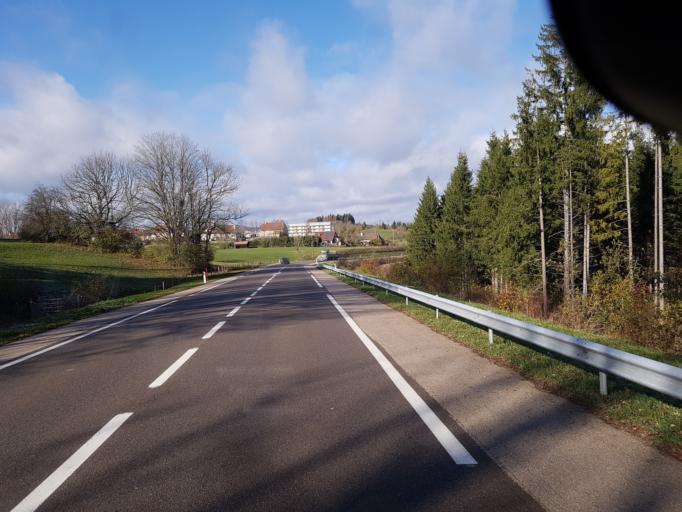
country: FR
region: Franche-Comte
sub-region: Departement du Jura
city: Morbier
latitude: 46.5787
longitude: 5.9630
